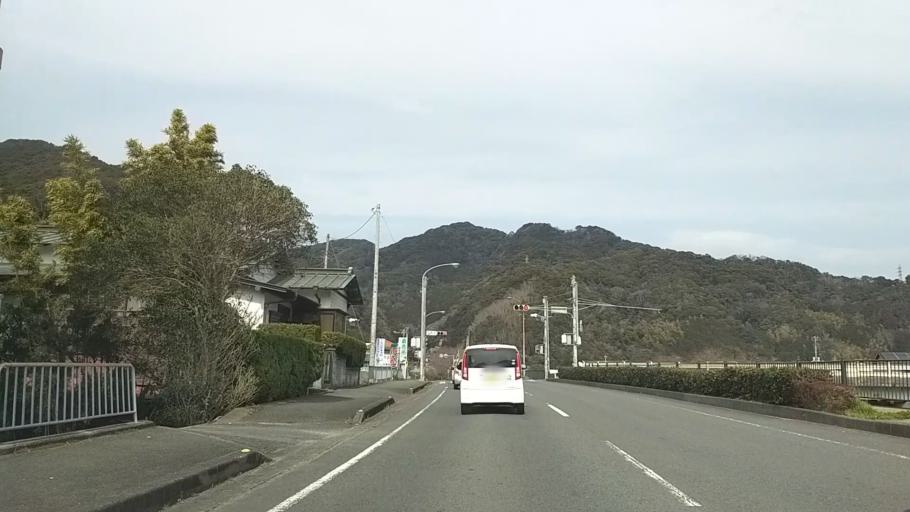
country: JP
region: Shizuoka
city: Shimoda
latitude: 34.7023
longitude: 138.9405
